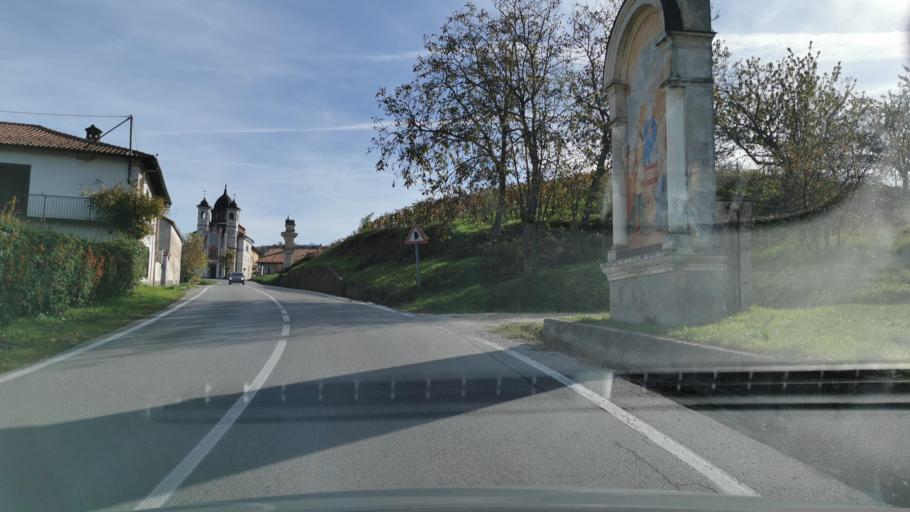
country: IT
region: Piedmont
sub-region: Provincia di Cuneo
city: Dogliani
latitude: 44.5200
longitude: 7.9522
